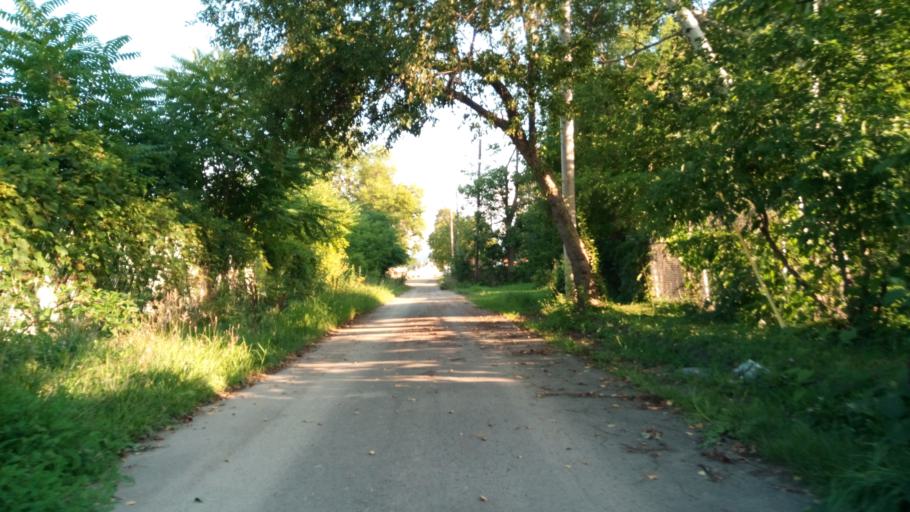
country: US
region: New York
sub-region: Chemung County
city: Elmira
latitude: 42.0954
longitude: -76.8021
